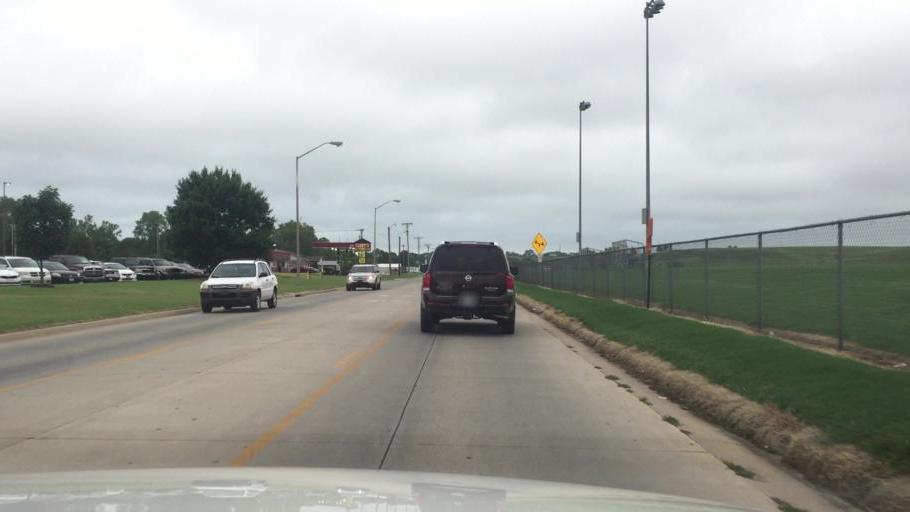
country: US
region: Kansas
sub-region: Montgomery County
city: Coffeyville
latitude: 37.0423
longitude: -95.6473
